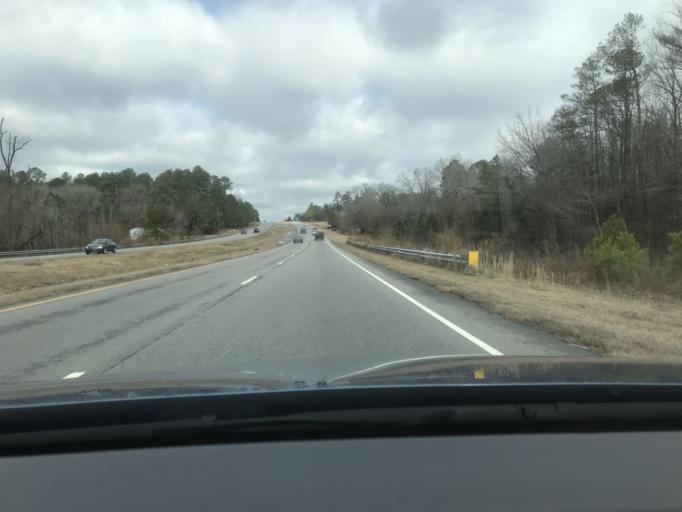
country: US
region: North Carolina
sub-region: Cumberland County
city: Spring Lake
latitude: 35.2858
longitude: -79.0753
